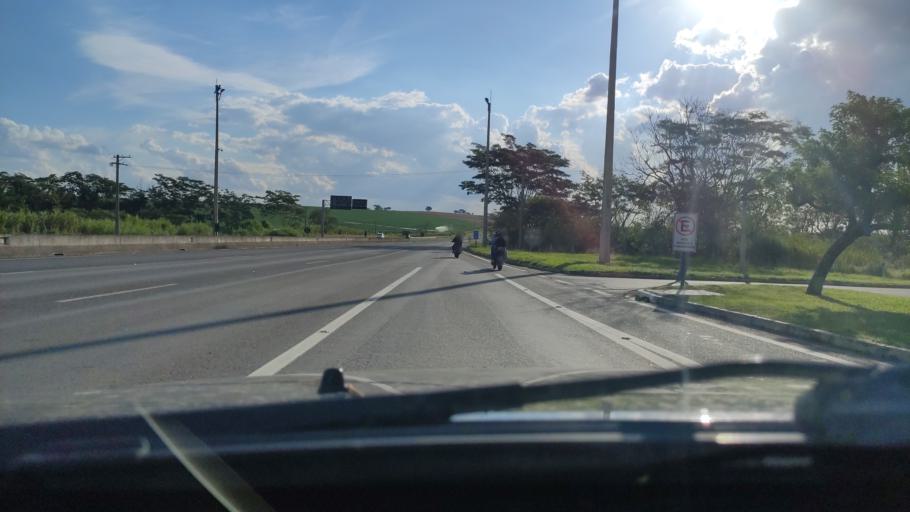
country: BR
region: Sao Paulo
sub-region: Mogi-Mirim
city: Mogi Mirim
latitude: -22.4566
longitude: -46.9026
